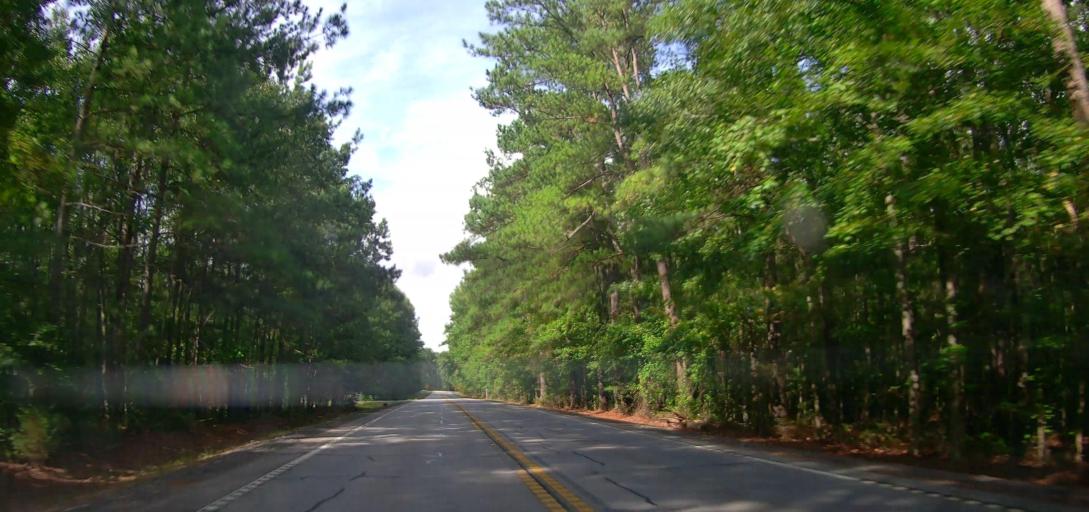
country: US
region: Georgia
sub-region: Harris County
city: Hamilton
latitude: 32.7927
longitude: -84.8702
